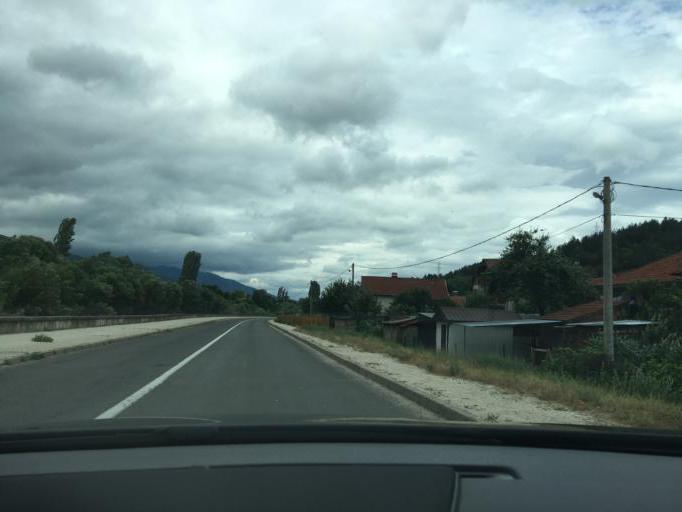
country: MK
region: Kriva Palanka
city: Kriva Palanka
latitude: 42.1995
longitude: 22.3241
